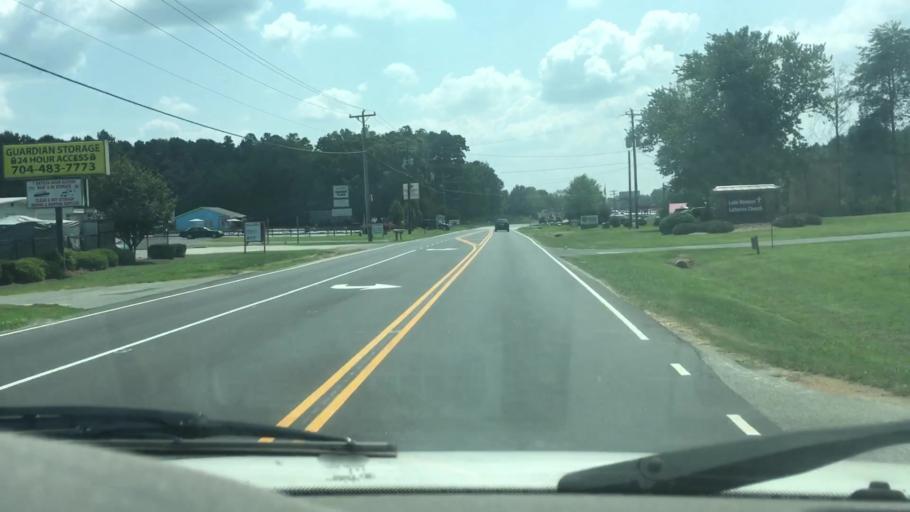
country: US
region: North Carolina
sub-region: Lincoln County
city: Westport
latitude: 35.4826
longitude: -80.9941
